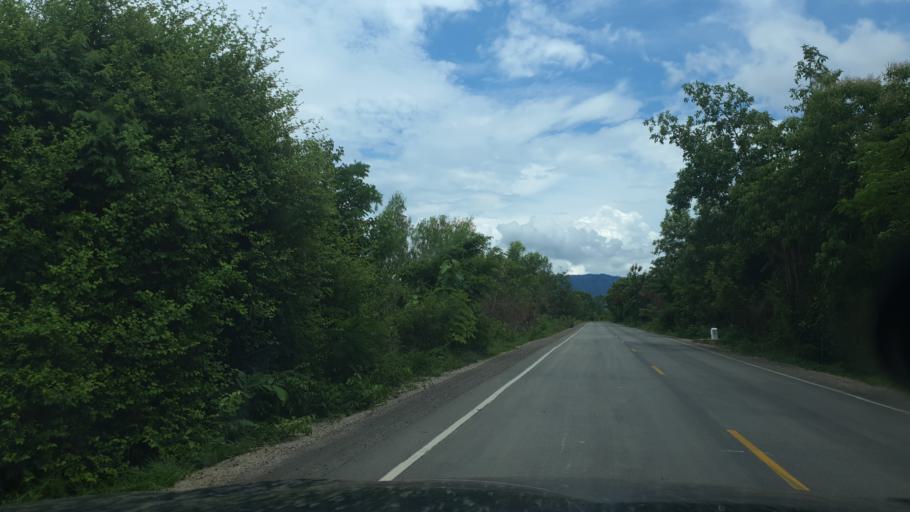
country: TH
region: Lampang
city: Sop Prap
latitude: 17.9247
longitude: 99.3809
